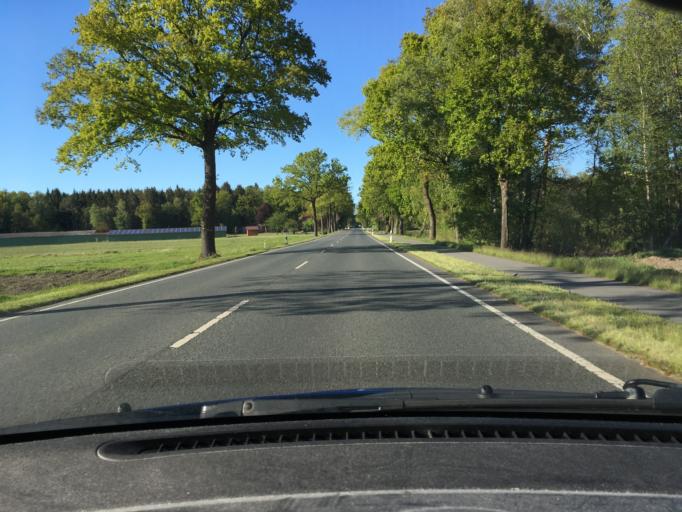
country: DE
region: Lower Saxony
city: Soltau
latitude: 53.0362
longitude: 9.8537
